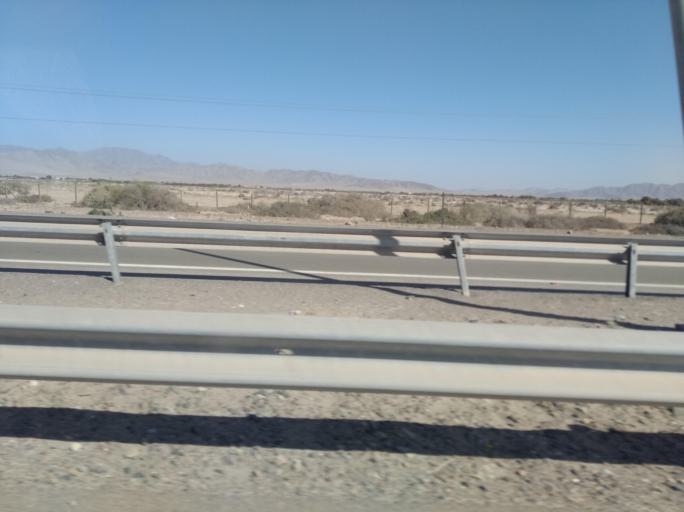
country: CL
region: Atacama
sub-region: Provincia de Copiapo
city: Copiapo
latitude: -27.3518
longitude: -70.6504
